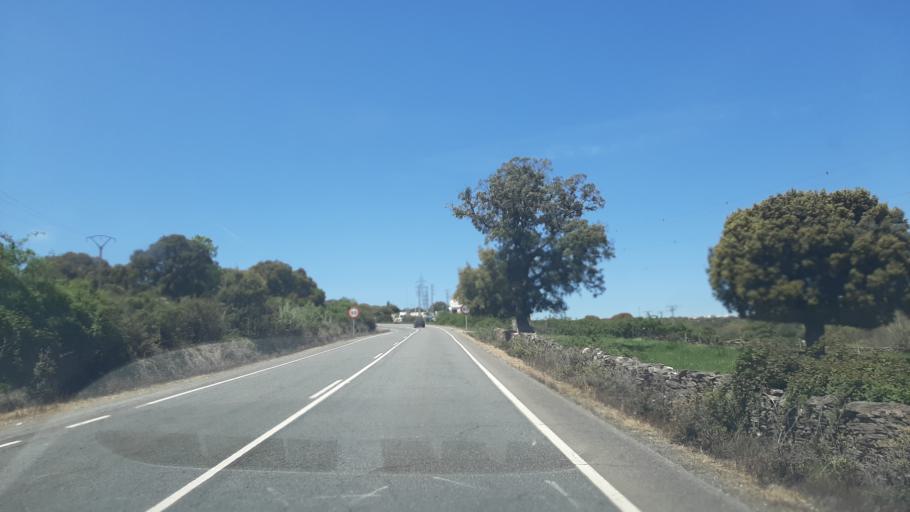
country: ES
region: Castille and Leon
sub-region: Provincia de Salamanca
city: Guijuelo
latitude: 40.5563
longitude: -5.6463
